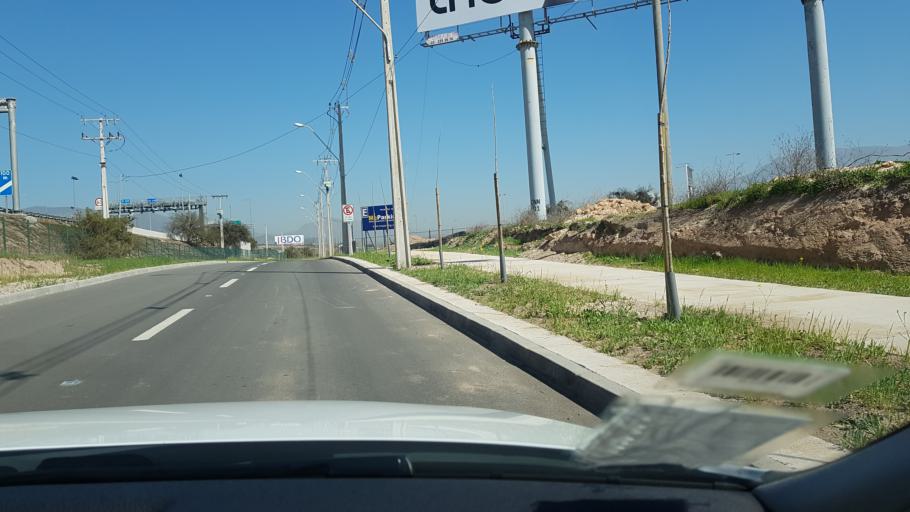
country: CL
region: Santiago Metropolitan
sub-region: Provincia de Santiago
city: Lo Prado
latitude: -33.4169
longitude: -70.7899
